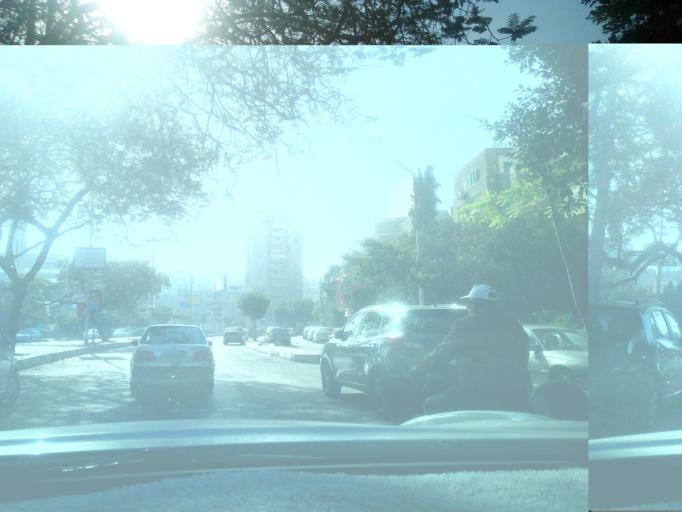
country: EG
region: Muhafazat al Qahirah
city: Cairo
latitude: 30.1015
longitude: 31.3233
